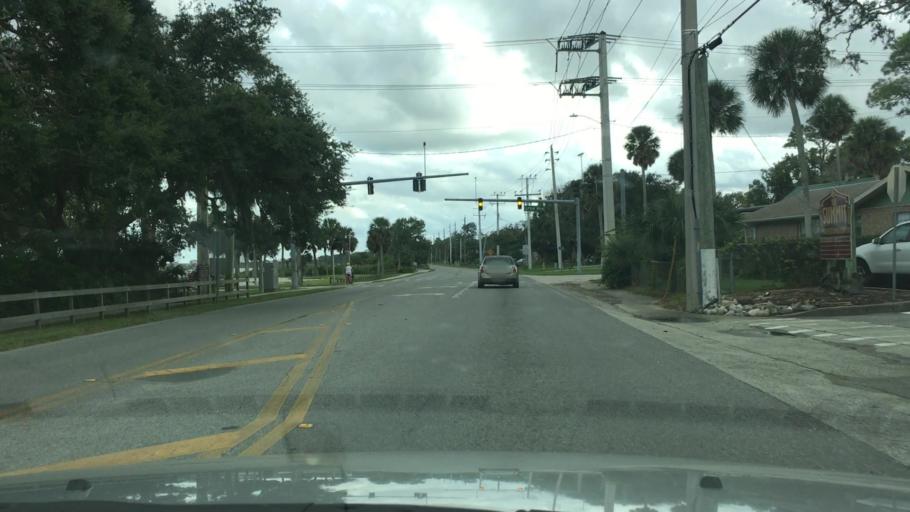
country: US
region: Florida
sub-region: Volusia County
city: Holly Hill
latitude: 29.2483
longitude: -81.0373
